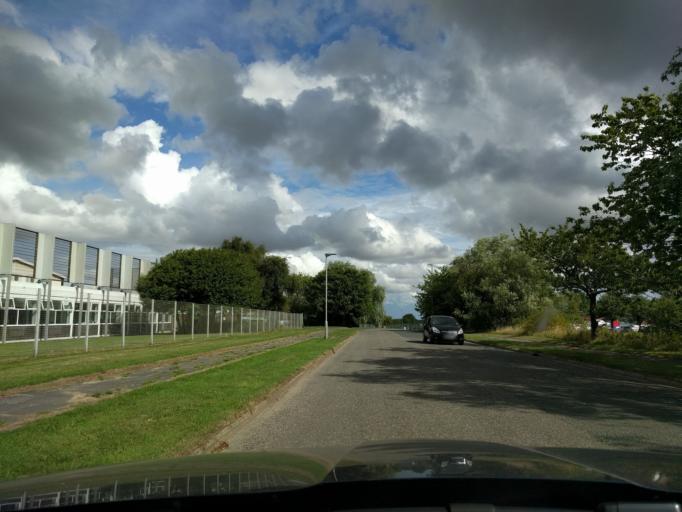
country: GB
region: England
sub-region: Northumberland
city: Cramlington
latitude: 55.0924
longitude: -1.6166
